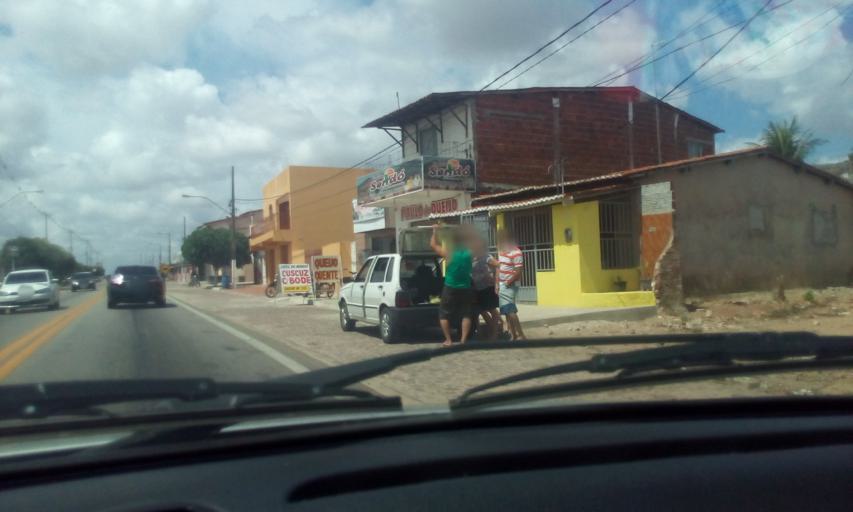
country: BR
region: Rio Grande do Norte
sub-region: Sao Paulo Do Potengi
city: Sao Paulo do Potengi
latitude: -5.9856
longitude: -35.5850
